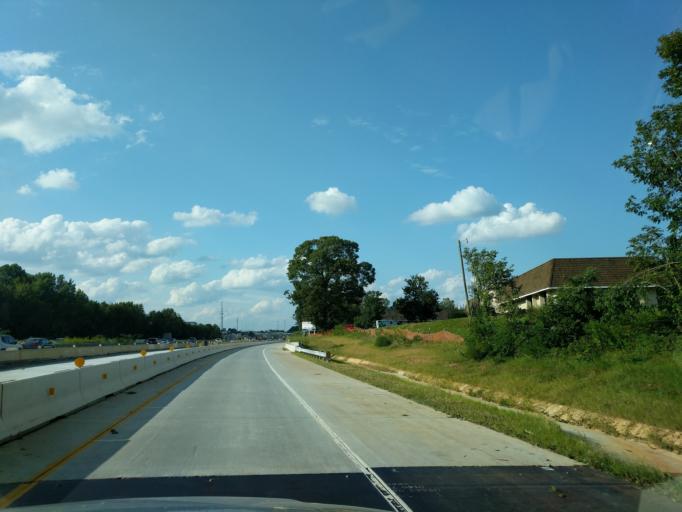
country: US
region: South Carolina
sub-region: Greenville County
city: Mauldin
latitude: 34.8166
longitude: -82.2900
